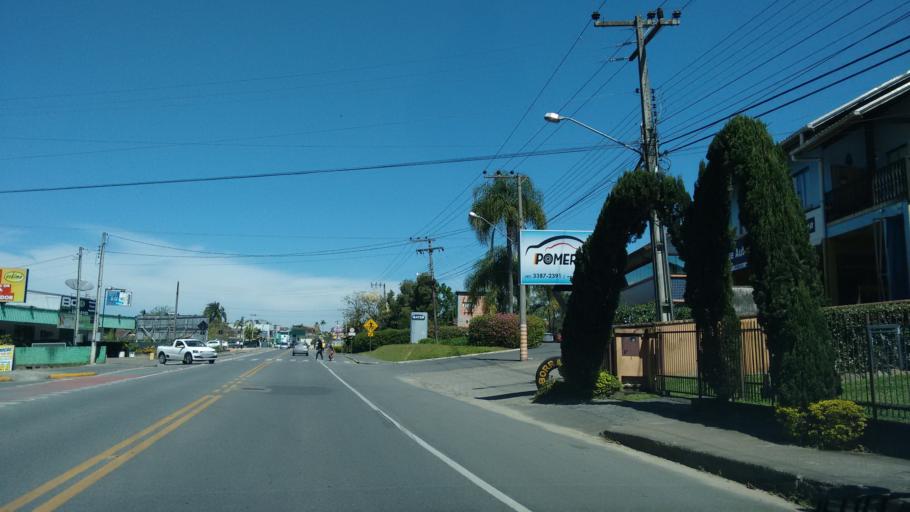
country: BR
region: Santa Catarina
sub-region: Pomerode
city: Pomerode
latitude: -26.7450
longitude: -49.1744
